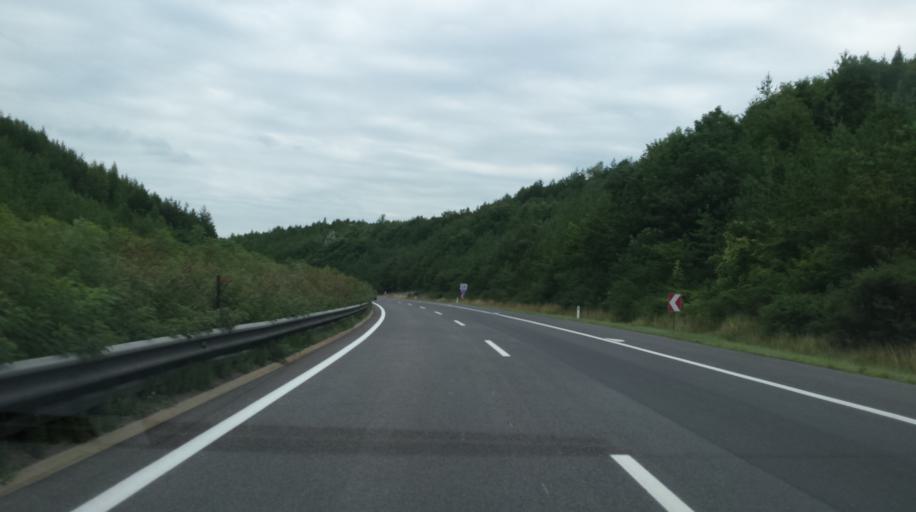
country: AT
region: Lower Austria
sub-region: Politischer Bezirk Baden
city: Heiligenkreuz
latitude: 48.0563
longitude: 16.1074
